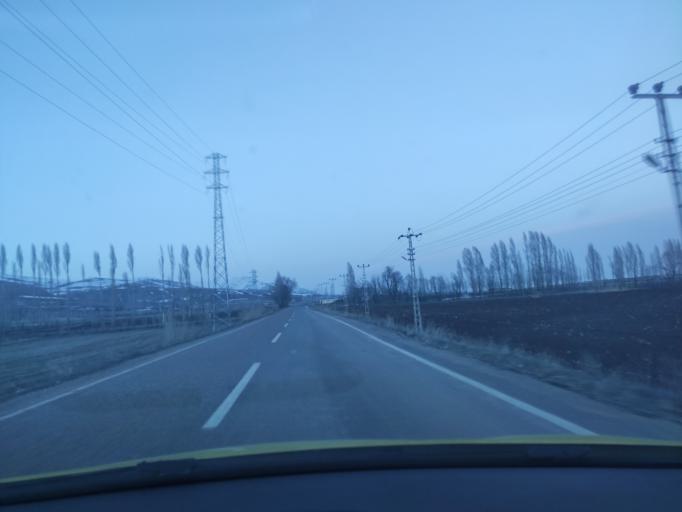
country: TR
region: Bayburt
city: Aydintepe
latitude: 40.3752
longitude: 40.1155
